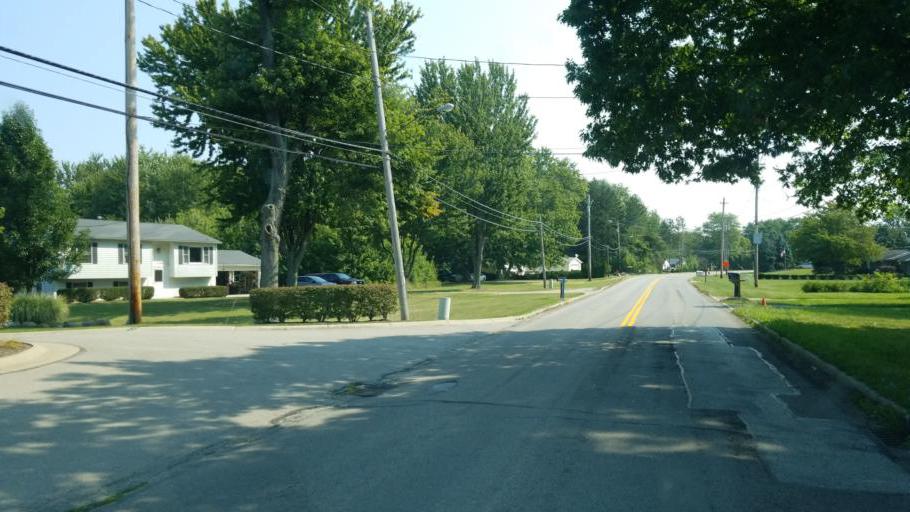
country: US
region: Ohio
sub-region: Lake County
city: Painesville
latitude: 41.7267
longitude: -81.1929
